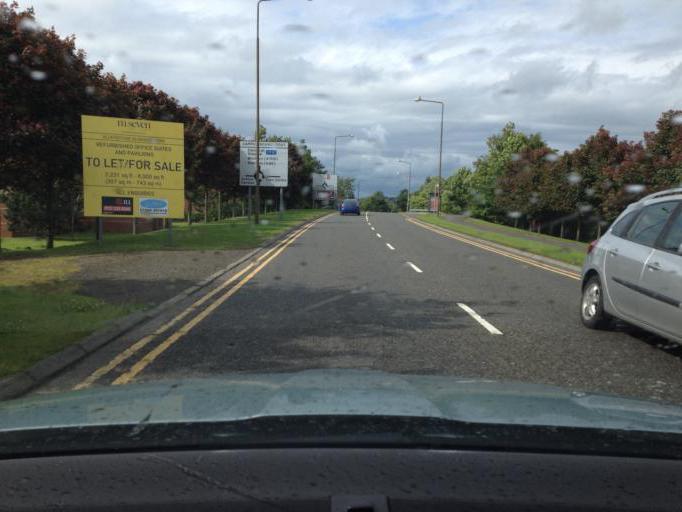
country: GB
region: Scotland
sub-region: West Lothian
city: Livingston
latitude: 55.8795
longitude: -3.5284
